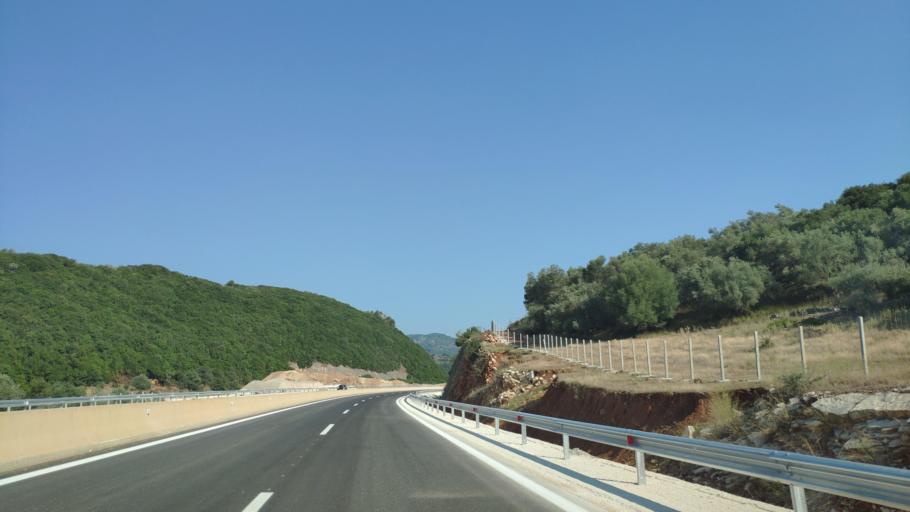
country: GR
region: West Greece
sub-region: Nomos Aitolias kai Akarnanias
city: Stanos
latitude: 38.7806
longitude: 21.1471
